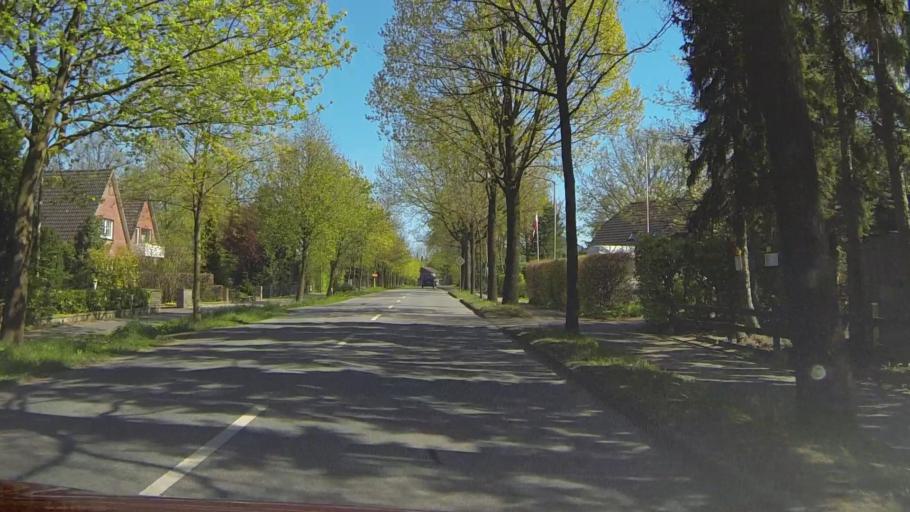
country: DE
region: Schleswig-Holstein
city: Kummerfeld
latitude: 53.6769
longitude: 9.7670
